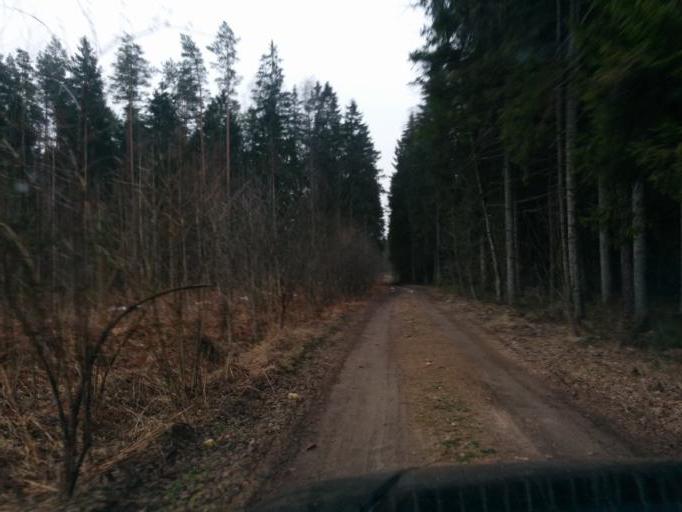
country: LV
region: Ikskile
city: Ikskile
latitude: 56.8071
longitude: 24.4825
